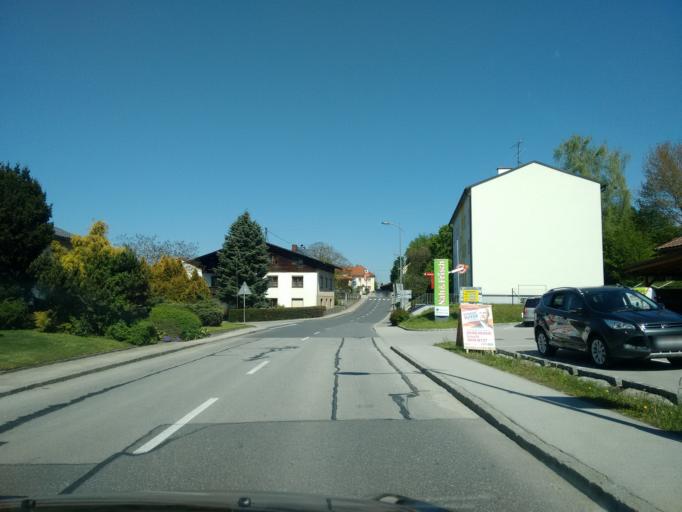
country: AT
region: Upper Austria
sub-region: Politischer Bezirk Steyr-Land
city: Waldneukirchen
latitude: 47.9977
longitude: 14.2608
